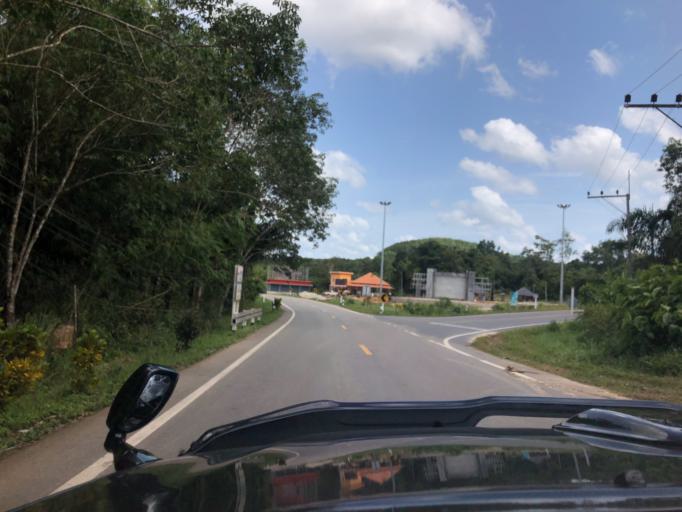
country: TH
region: Krabi
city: Khlong Thom
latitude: 7.9497
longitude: 99.2057
